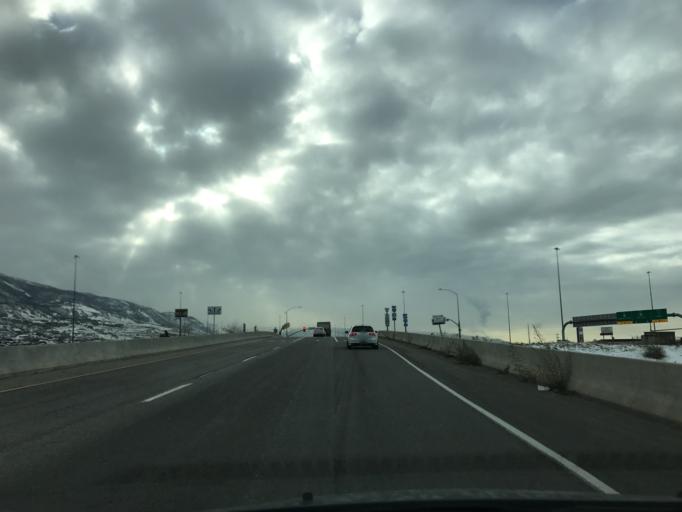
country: US
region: Utah
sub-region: Davis County
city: Farmington
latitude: 40.9922
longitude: -111.9039
